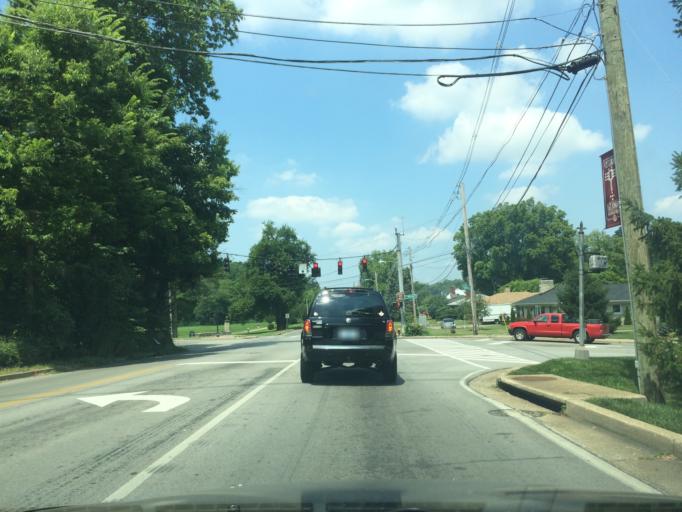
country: US
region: Kentucky
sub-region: Jefferson County
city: Audubon Park
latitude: 38.2135
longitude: -85.7007
